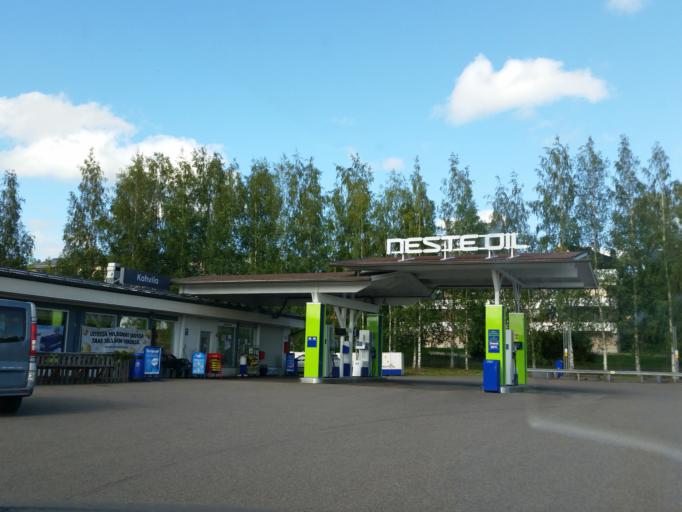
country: FI
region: Uusimaa
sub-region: Helsinki
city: Saukkola
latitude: 60.4729
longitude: 23.9800
